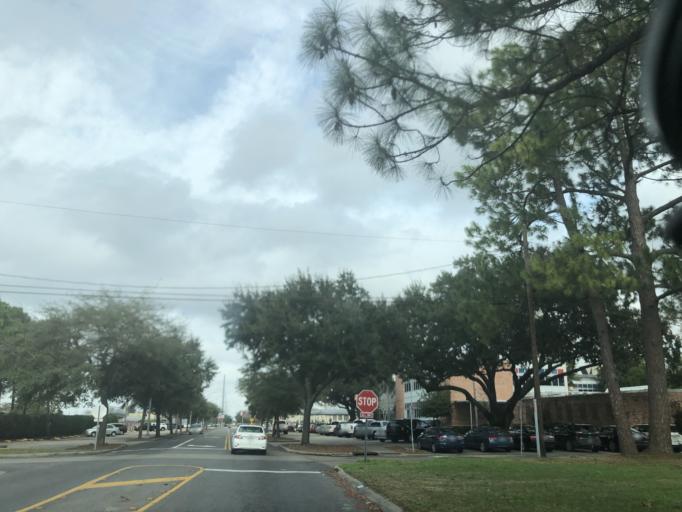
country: US
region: Louisiana
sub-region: Jefferson Parish
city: Metairie
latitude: 29.9891
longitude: -90.1600
